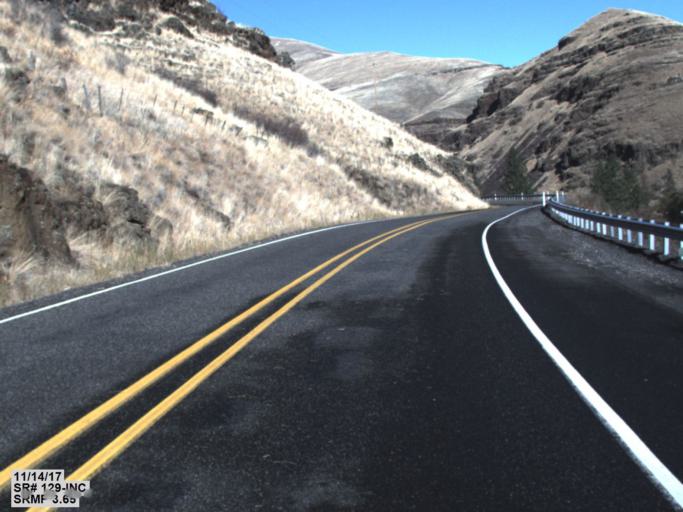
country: US
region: Washington
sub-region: Asotin County
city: Asotin
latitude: 46.0321
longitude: -117.2558
